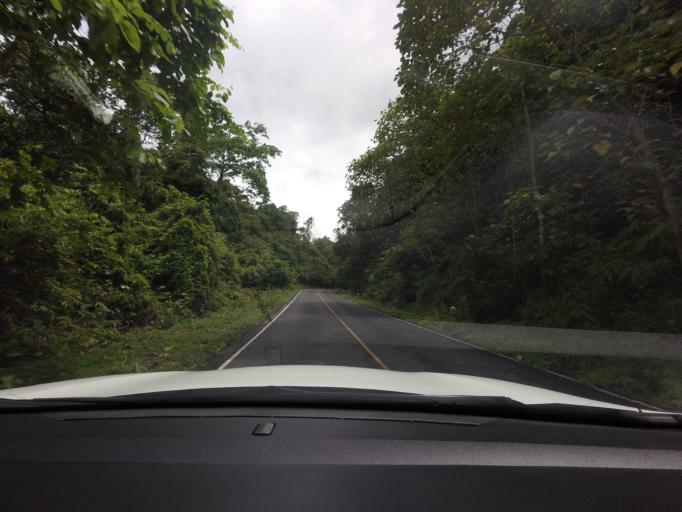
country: TH
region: Nakhon Nayok
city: Nakhon Nayok
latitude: 14.3529
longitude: 101.3431
